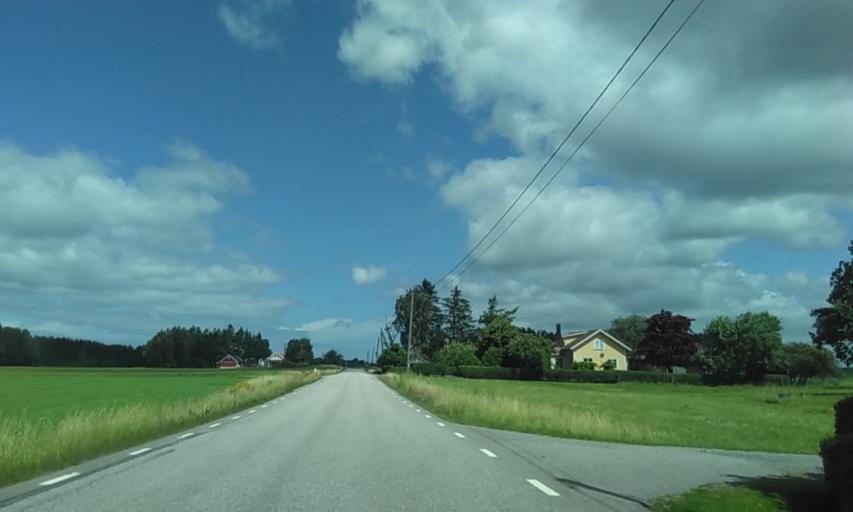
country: SE
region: Vaestra Goetaland
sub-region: Grastorps Kommun
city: Graestorp
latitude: 58.3661
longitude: 12.6839
